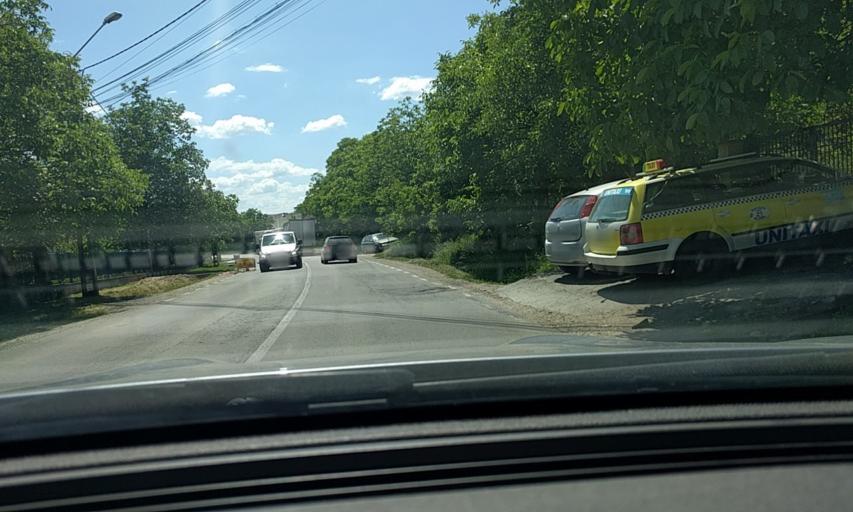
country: RO
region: Bistrita-Nasaud
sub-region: Municipiul Bistrita
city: Viisoara
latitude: 47.1121
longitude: 24.4549
